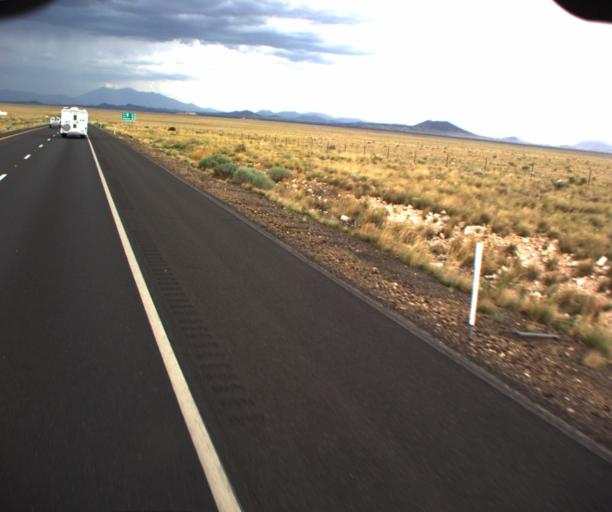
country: US
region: Arizona
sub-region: Coconino County
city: LeChee
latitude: 35.1342
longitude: -111.1973
